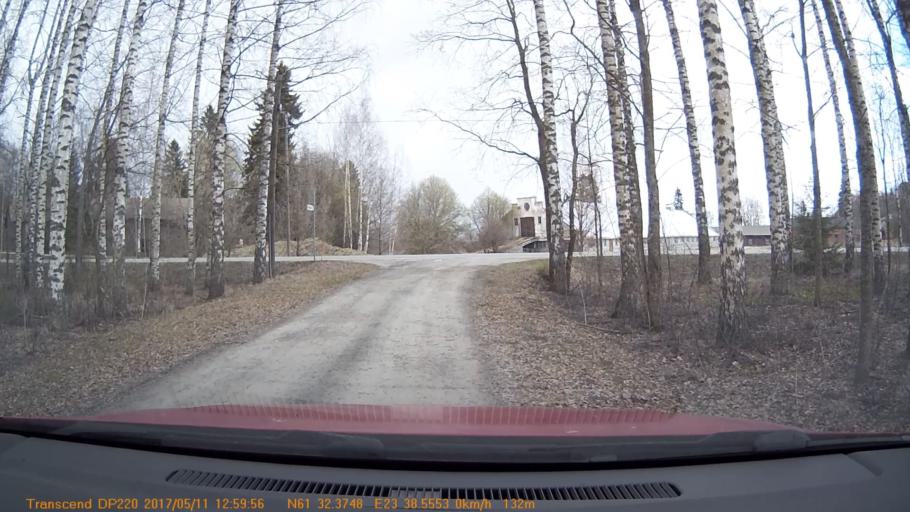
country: FI
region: Pirkanmaa
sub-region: Tampere
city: Yloejaervi
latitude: 61.5396
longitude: 23.6426
